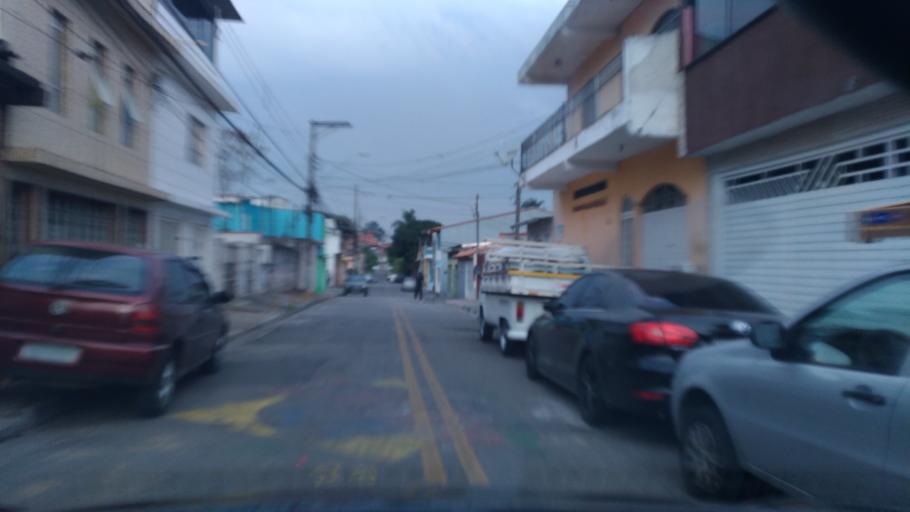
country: BR
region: Sao Paulo
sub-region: Itaquaquecetuba
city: Itaquaquecetuba
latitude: -23.4326
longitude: -46.4276
